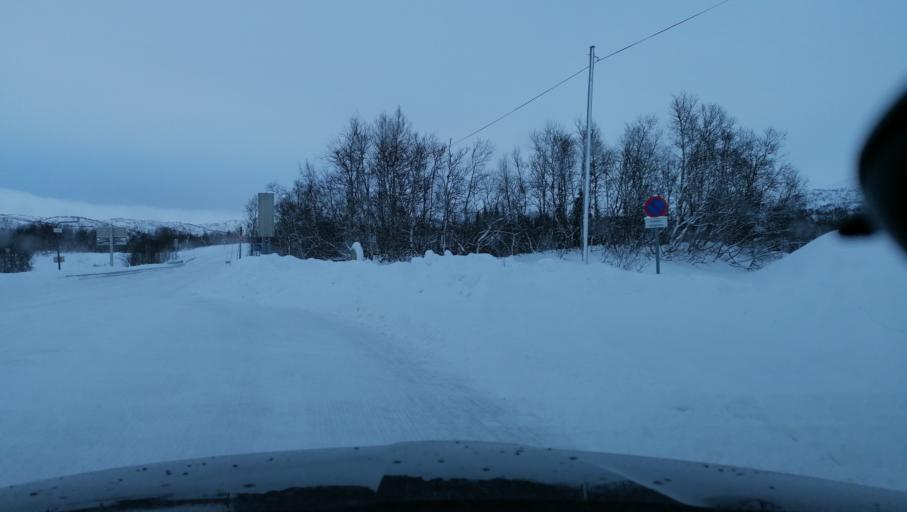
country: NO
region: Aust-Agder
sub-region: Bykle
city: Hovden
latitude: 59.6447
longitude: 7.4609
